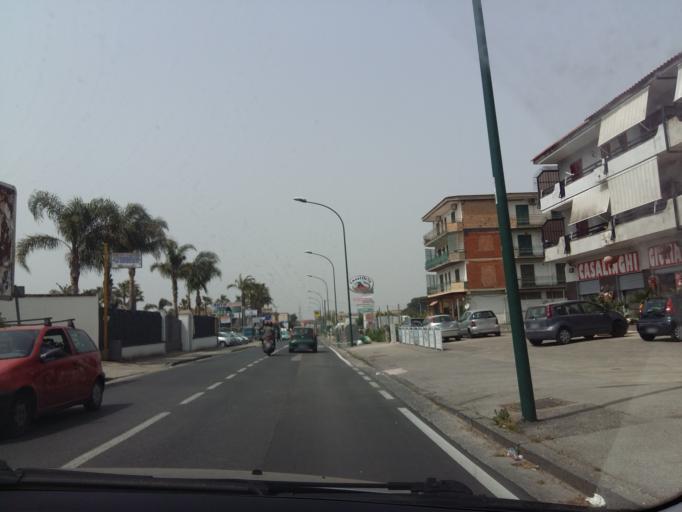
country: IT
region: Campania
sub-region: Provincia di Napoli
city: Mugnano di Napoli
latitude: 40.8948
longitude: 14.2160
